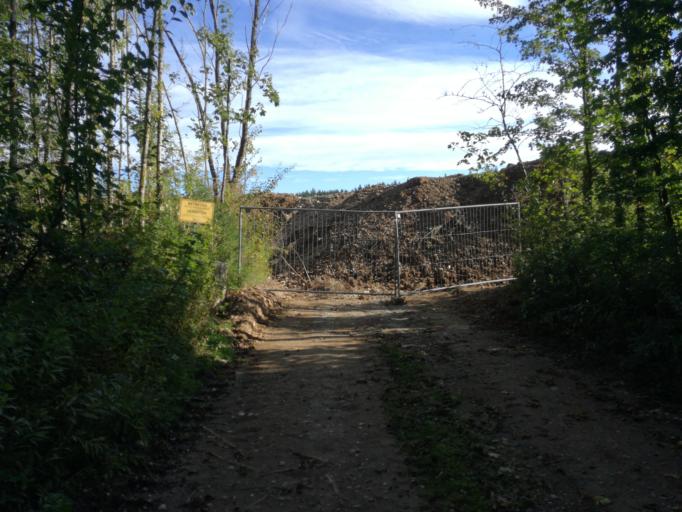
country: DE
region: Bavaria
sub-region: Upper Bavaria
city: Planegg
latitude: 48.0922
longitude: 11.4311
